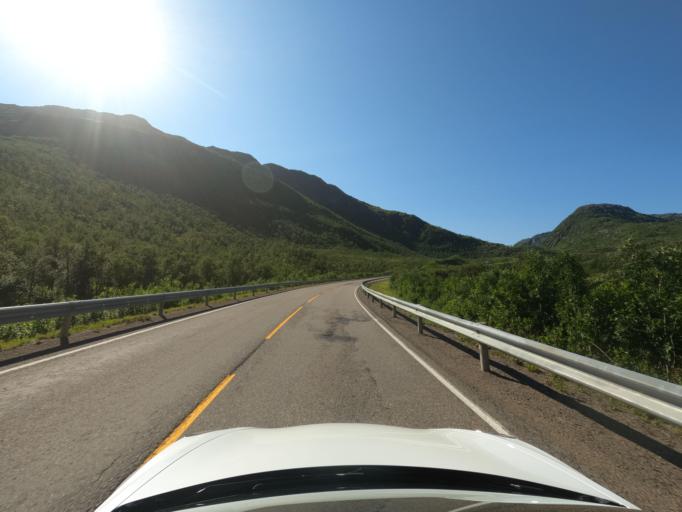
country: NO
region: Nordland
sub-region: Lodingen
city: Lodingen
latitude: 68.4940
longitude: 15.7000
